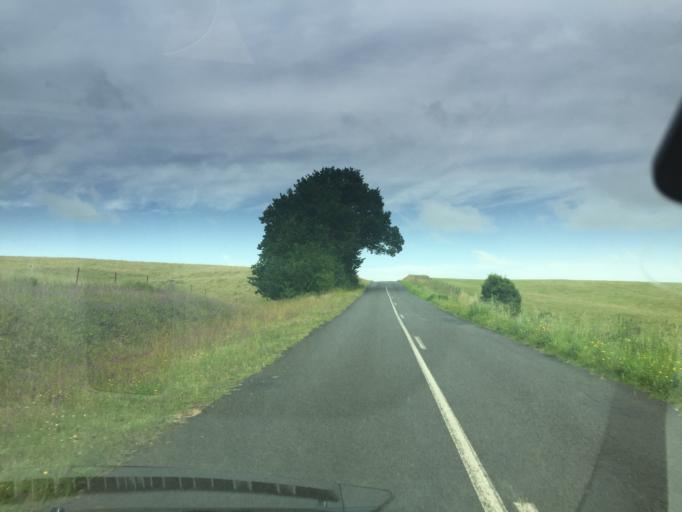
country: AU
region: New South Wales
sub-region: Bega Valley
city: Bega
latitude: -36.7495
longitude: 149.6648
